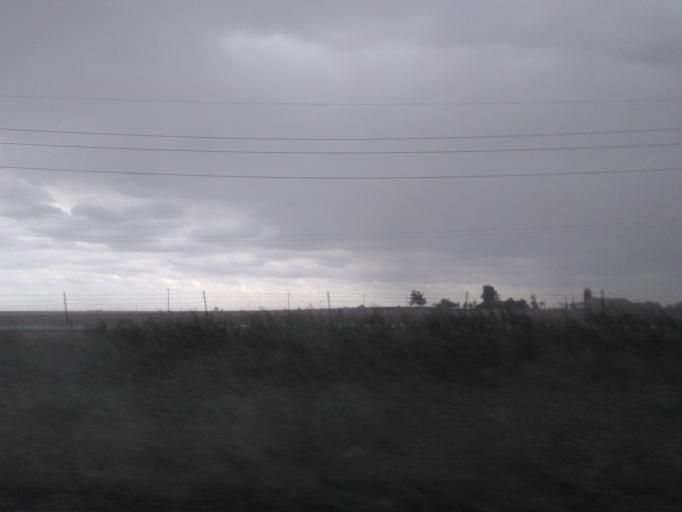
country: US
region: Illinois
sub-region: Madison County
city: Highland
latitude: 38.8116
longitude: -89.5751
